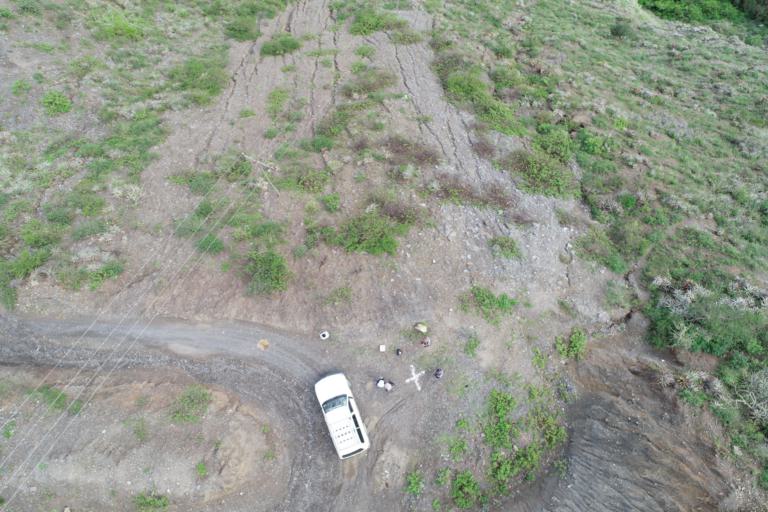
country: BO
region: La Paz
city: Sorata
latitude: -15.5132
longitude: -68.6628
